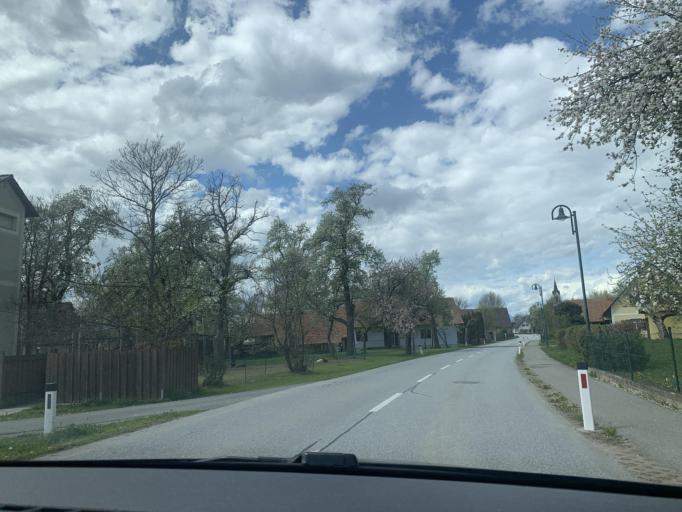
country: AT
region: Styria
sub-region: Politischer Bezirk Graz-Umgebung
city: Wundschuh
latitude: 46.9080
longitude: 15.4160
